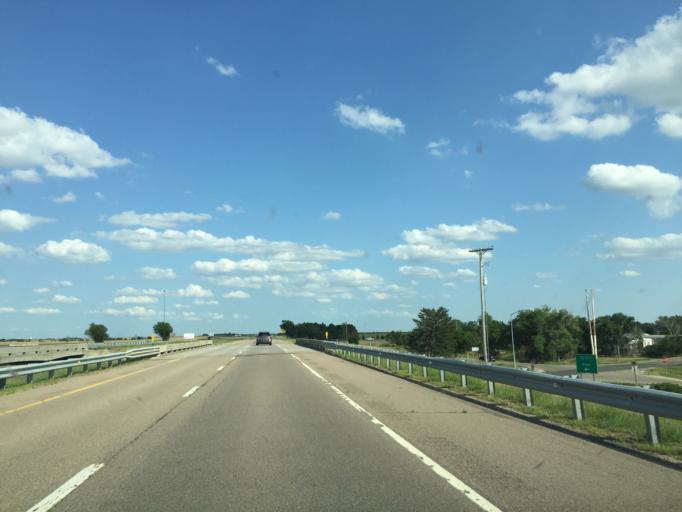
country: US
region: Kansas
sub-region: Gove County
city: Gove
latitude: 39.0582
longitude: -100.2424
